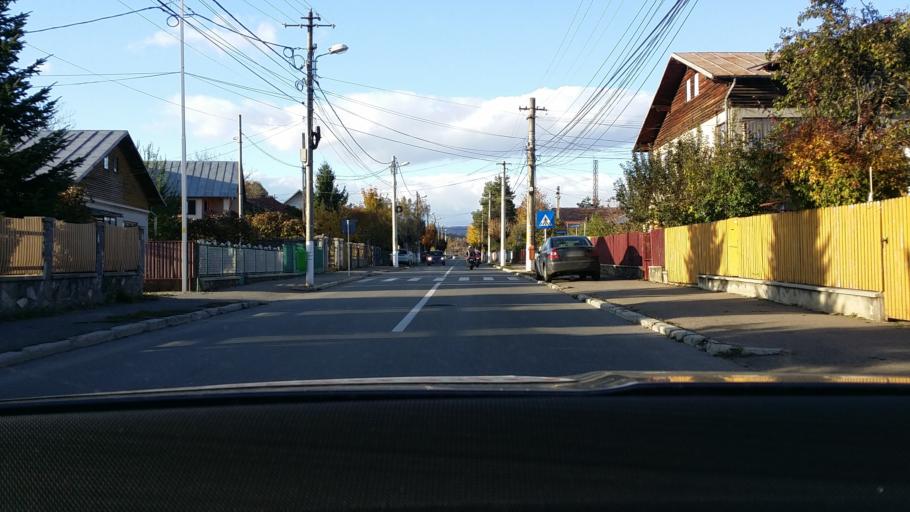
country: RO
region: Prahova
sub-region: Municipiul Campina
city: Campina
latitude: 45.1413
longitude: 25.7344
